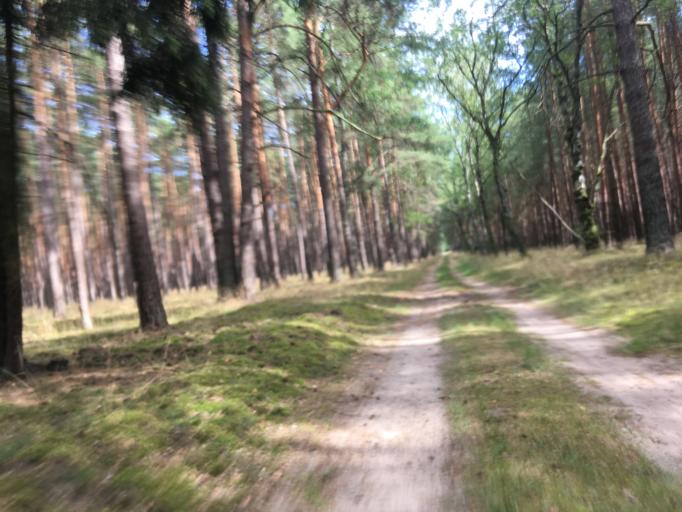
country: DE
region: Brandenburg
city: Rheinsberg
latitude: 53.0364
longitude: 12.9188
